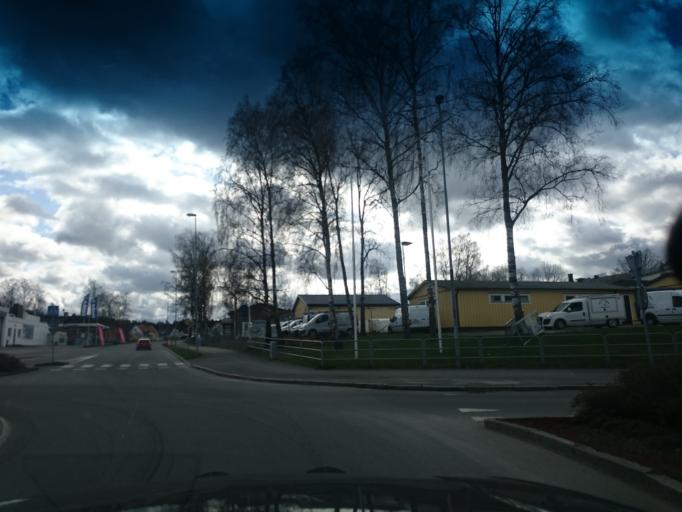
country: SE
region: Joenkoeping
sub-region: Vetlanda Kommun
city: Vetlanda
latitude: 57.4214
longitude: 15.0805
